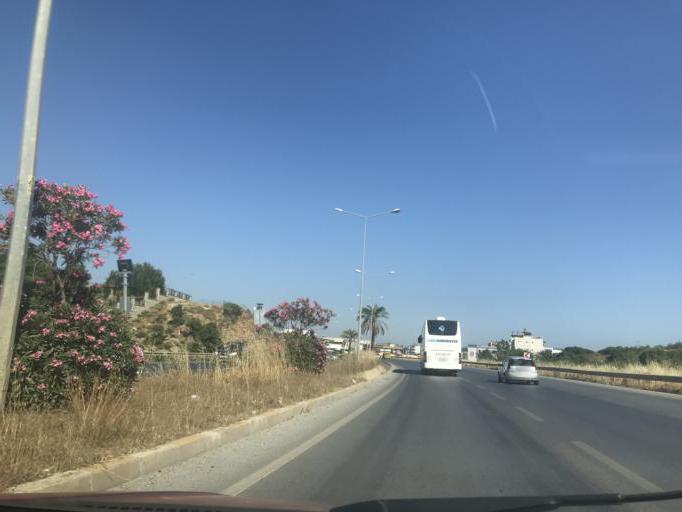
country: TR
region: Antalya
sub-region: Manavgat
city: Manavgat
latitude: 36.7842
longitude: 31.4167
